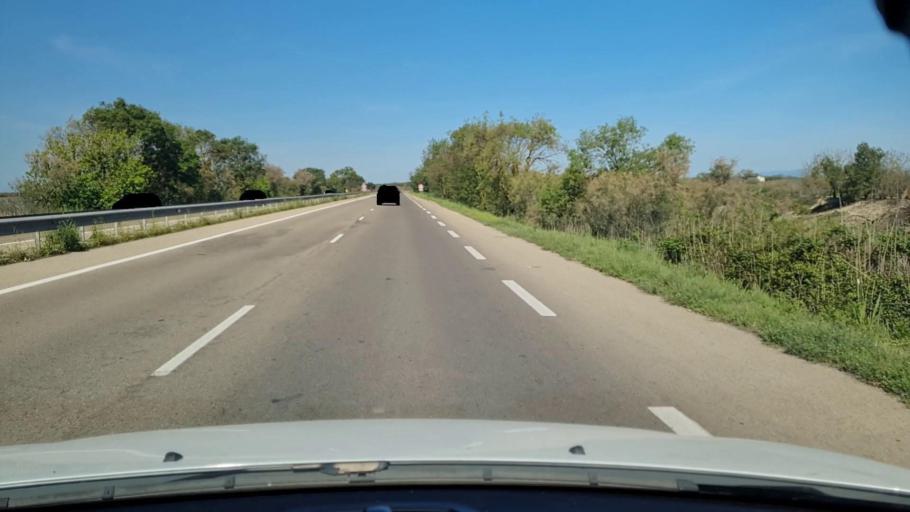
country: FR
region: Languedoc-Roussillon
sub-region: Departement du Gard
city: Le Grau-du-Roi
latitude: 43.5621
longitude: 4.1402
